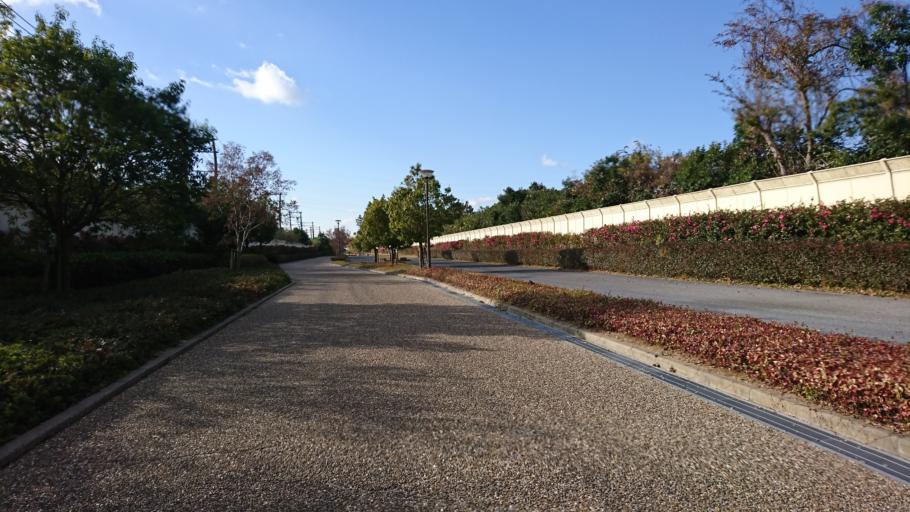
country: JP
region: Hyogo
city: Kakogawacho-honmachi
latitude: 34.7500
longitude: 134.7815
